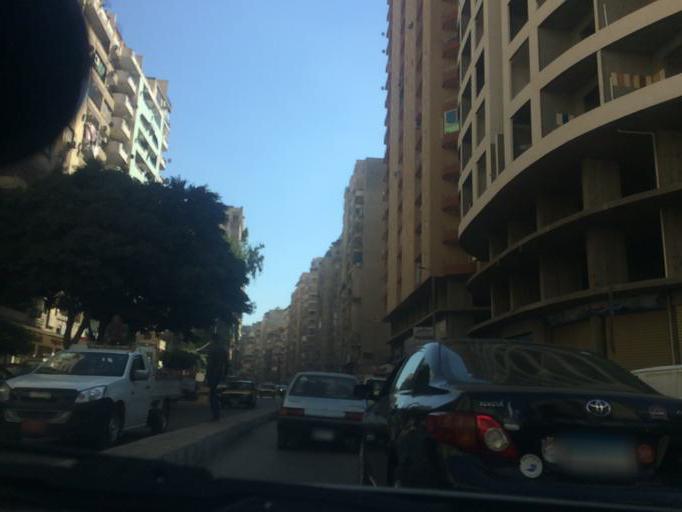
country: EG
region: Alexandria
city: Alexandria
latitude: 31.2730
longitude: 30.0043
